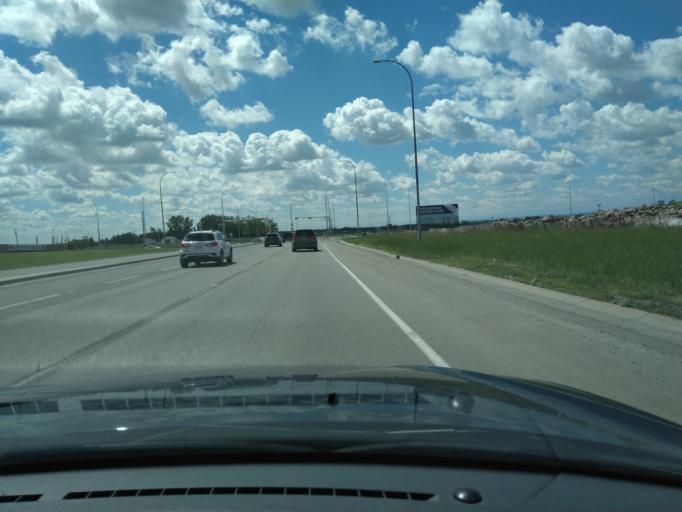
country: CA
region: Alberta
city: Calgary
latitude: 51.1341
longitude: -113.9703
